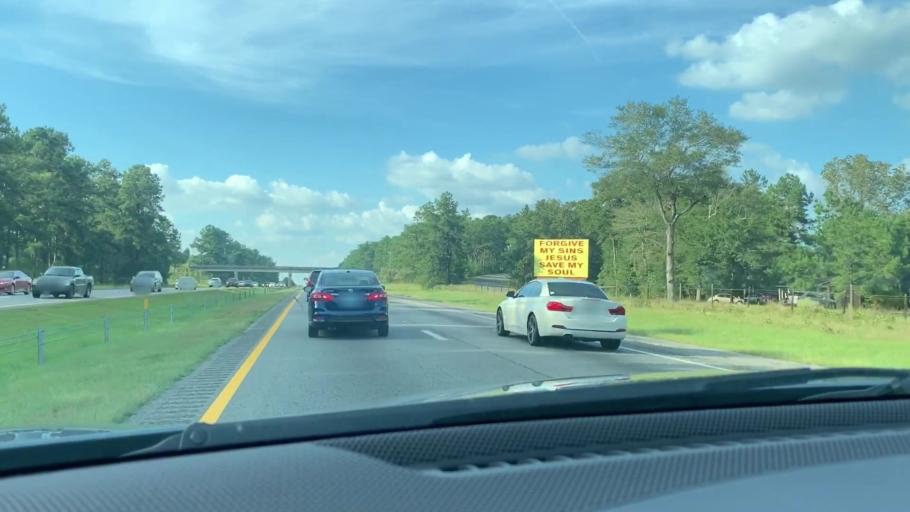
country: US
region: South Carolina
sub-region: Calhoun County
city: Saint Matthews
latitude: 33.6082
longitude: -80.8632
